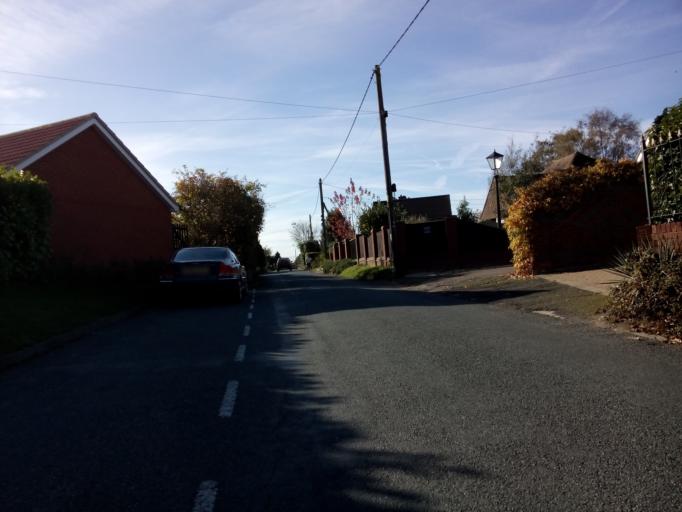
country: GB
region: England
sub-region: Suffolk
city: Bramford
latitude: 52.0285
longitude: 1.1081
